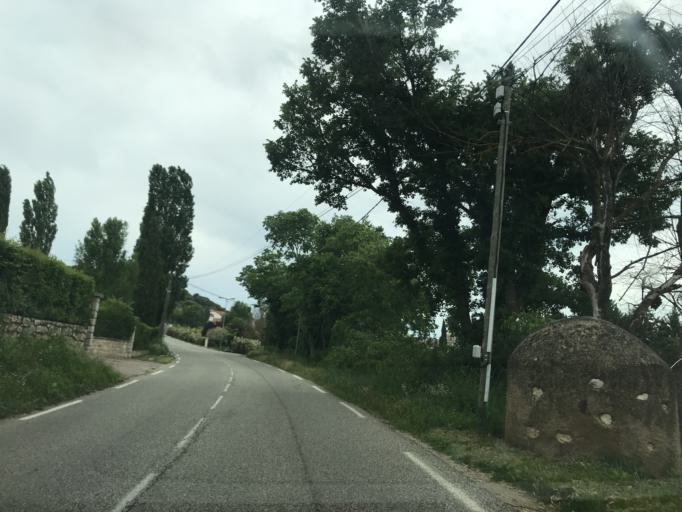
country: FR
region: Provence-Alpes-Cote d'Azur
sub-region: Departement du Var
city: Ginasservis
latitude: 43.6645
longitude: 5.8530
